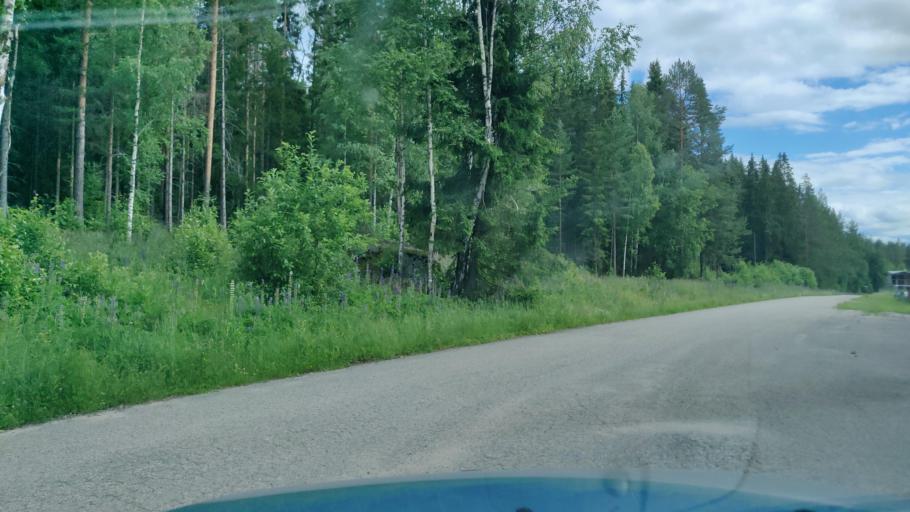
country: SE
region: Vaermland
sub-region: Hagfors Kommun
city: Hagfors
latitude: 60.0468
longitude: 13.7120
